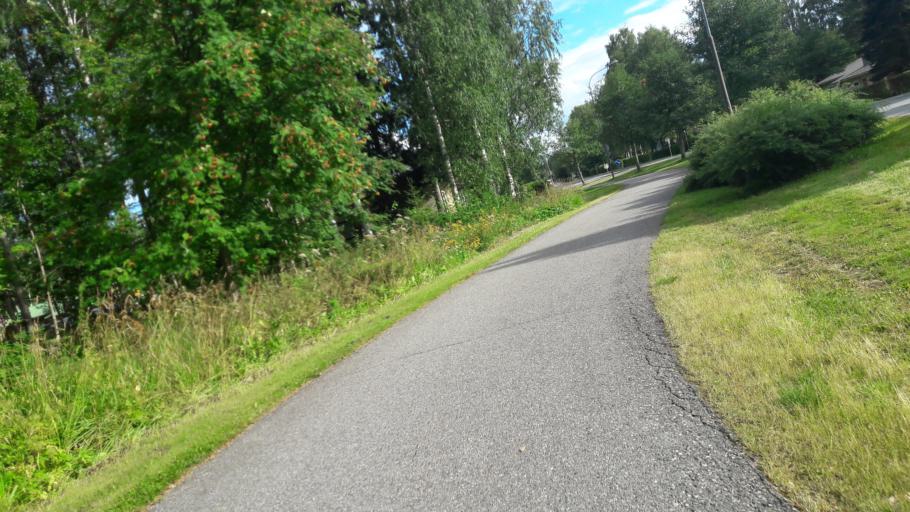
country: FI
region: North Karelia
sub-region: Joensuu
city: Joensuu
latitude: 62.6102
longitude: 29.7376
